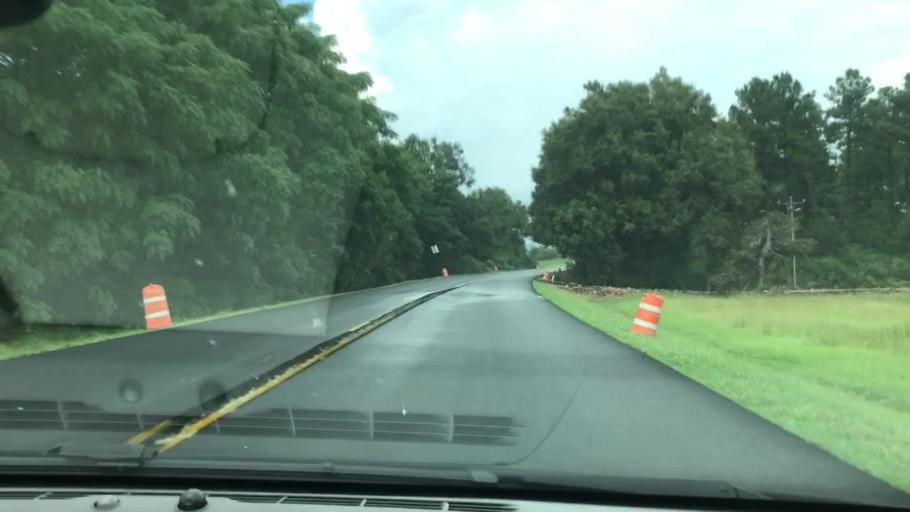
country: US
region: Georgia
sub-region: Early County
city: Blakely
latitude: 31.4063
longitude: -84.9612
